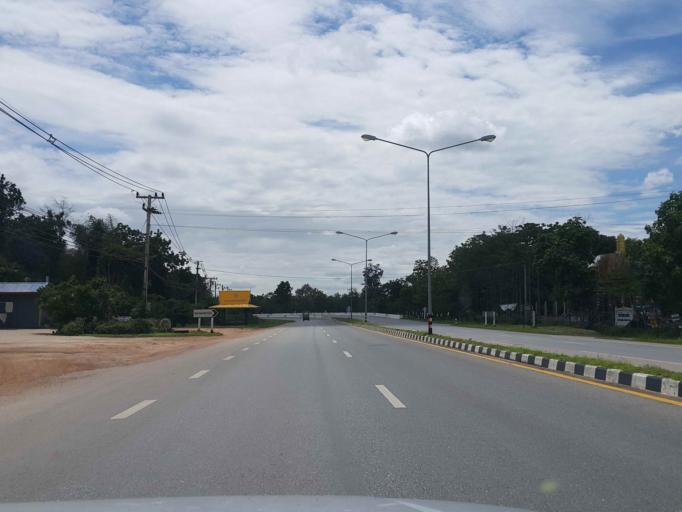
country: TH
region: Sukhothai
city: Ban Dan Lan Hoi
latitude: 16.9962
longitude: 99.4950
